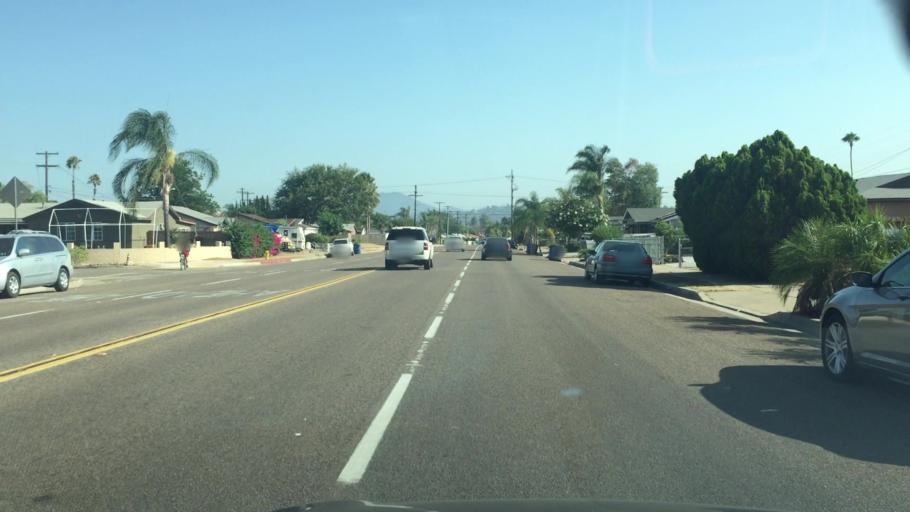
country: US
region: California
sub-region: San Diego County
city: Bostonia
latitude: 32.8186
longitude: -116.9497
